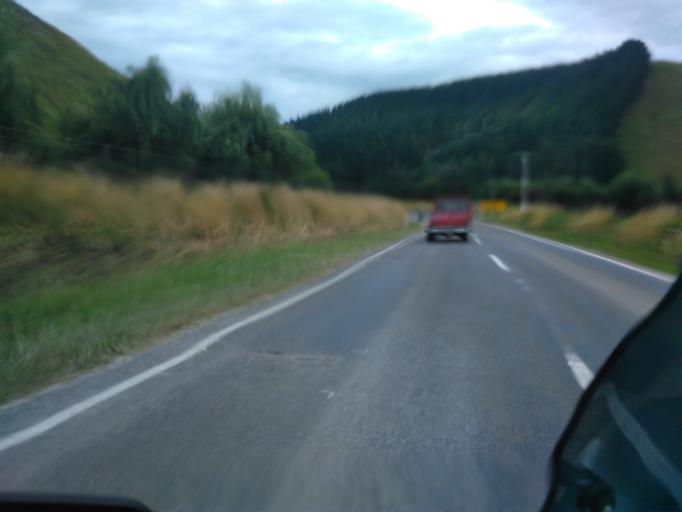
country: NZ
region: Gisborne
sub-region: Gisborne District
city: Gisborne
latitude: -38.4611
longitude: 177.7438
